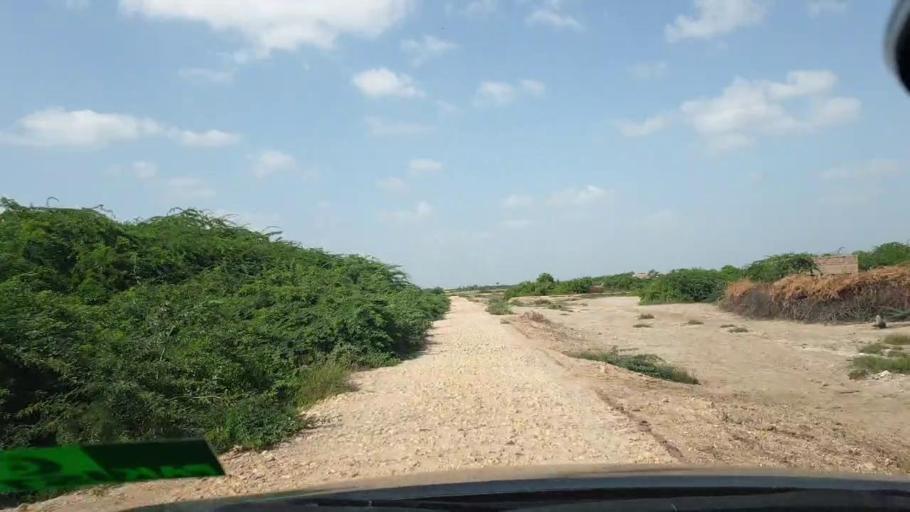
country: PK
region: Sindh
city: Tando Bago
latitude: 24.6637
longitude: 69.2040
